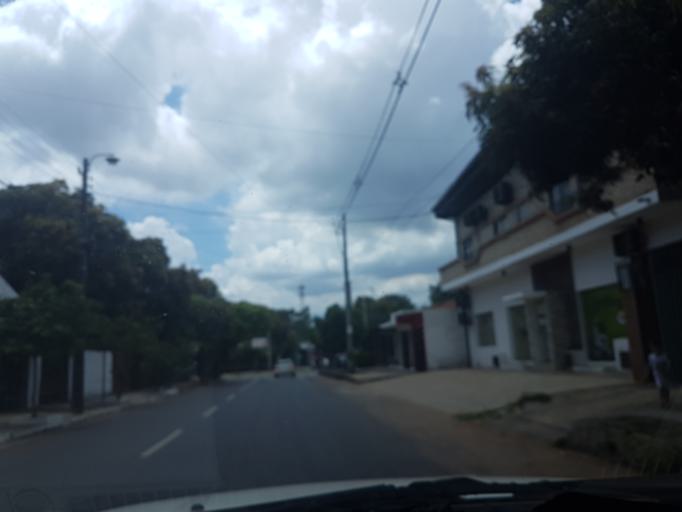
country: PY
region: Central
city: Fernando de la Mora
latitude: -25.3158
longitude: -57.5591
